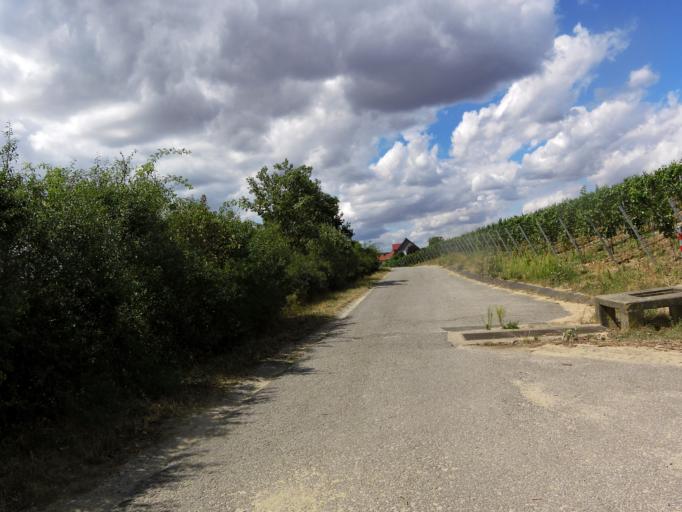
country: DE
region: Bavaria
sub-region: Regierungsbezirk Unterfranken
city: Eibelstadt
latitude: 49.7224
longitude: 10.0142
